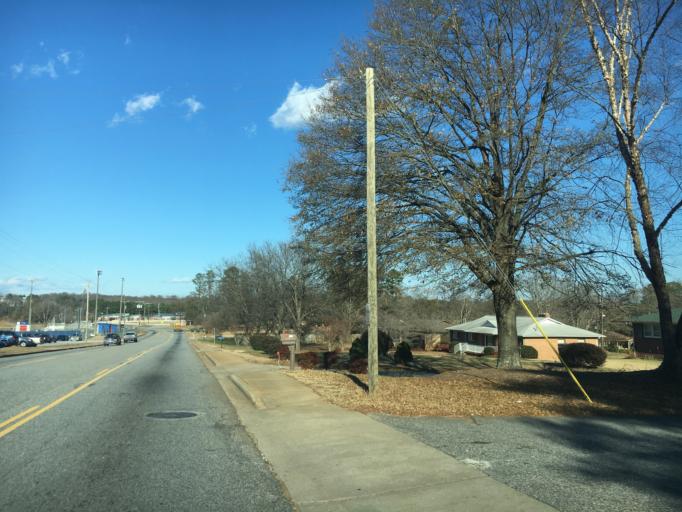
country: US
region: South Carolina
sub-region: Spartanburg County
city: Lyman
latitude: 34.9326
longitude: -82.1253
